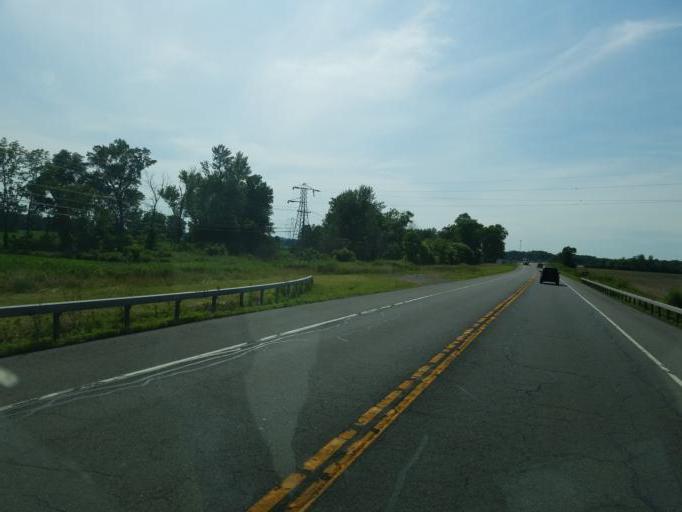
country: US
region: New York
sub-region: Livingston County
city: Avon
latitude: 42.9183
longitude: -77.7580
